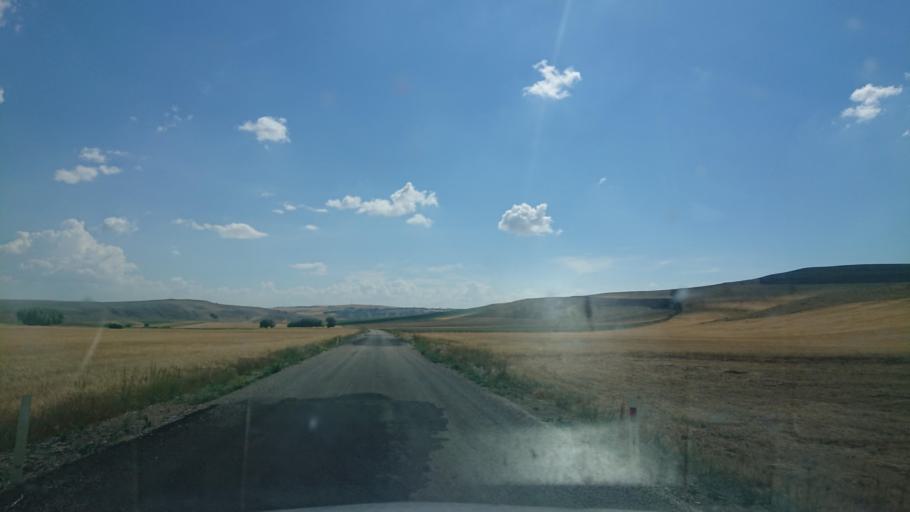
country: TR
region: Aksaray
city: Agacoren
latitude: 38.7971
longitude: 33.8212
